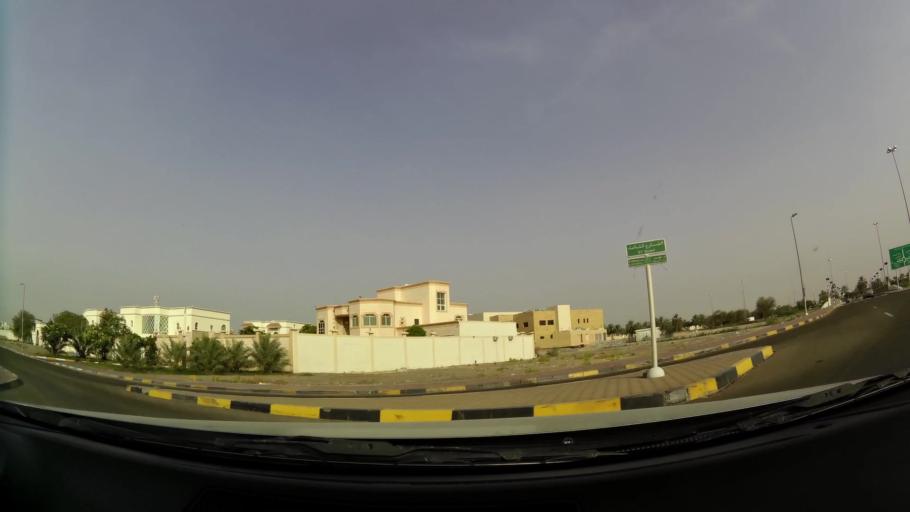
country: AE
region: Abu Dhabi
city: Al Ain
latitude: 24.2144
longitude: 55.6654
